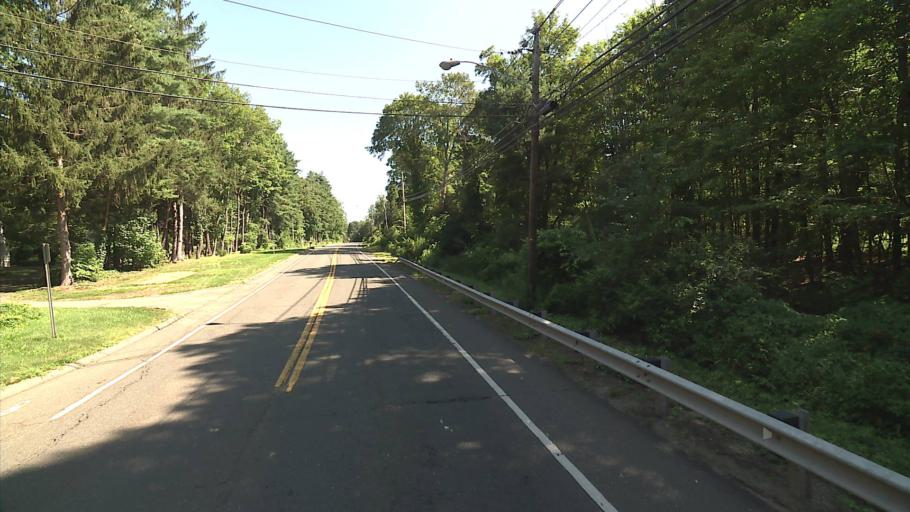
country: US
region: Connecticut
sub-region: Hartford County
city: Weatogue
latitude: 41.7882
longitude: -72.8164
